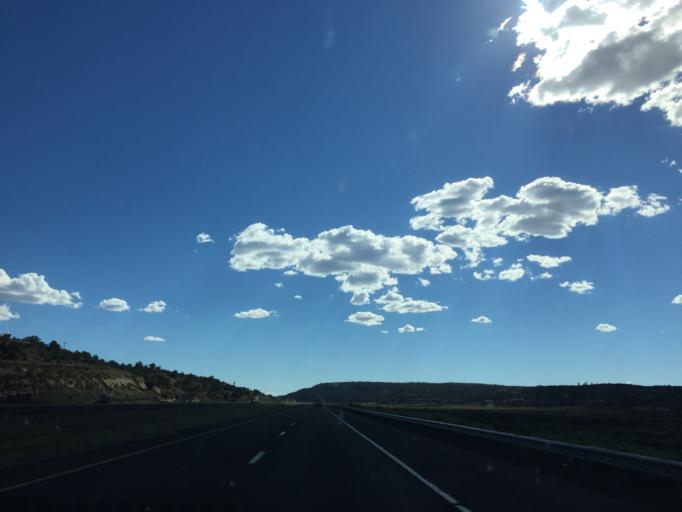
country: US
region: New Mexico
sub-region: McKinley County
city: Gallup
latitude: 35.4746
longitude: -108.9239
